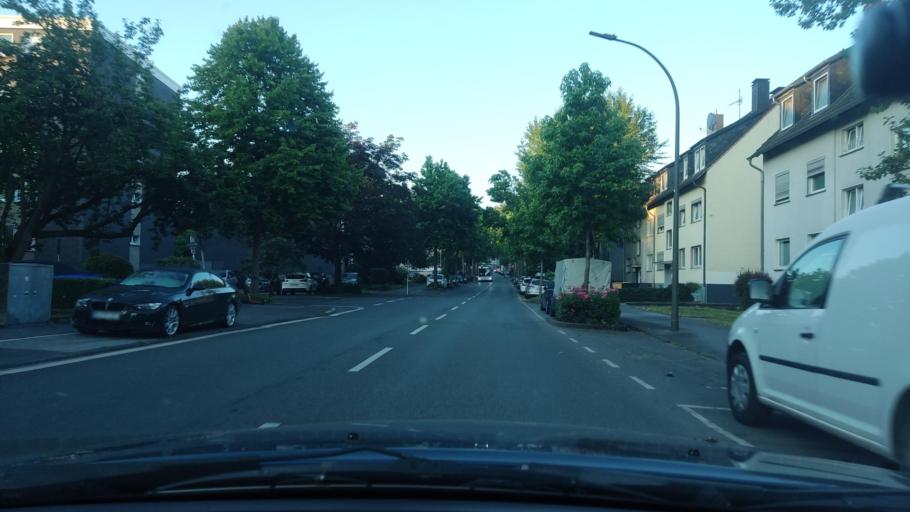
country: DE
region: North Rhine-Westphalia
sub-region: Regierungsbezirk Arnsberg
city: Dortmund
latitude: 51.5158
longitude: 7.4240
